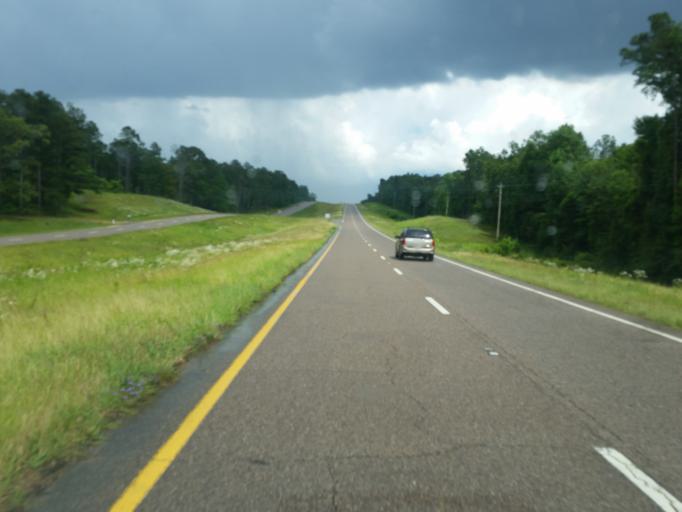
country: US
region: Mississippi
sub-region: George County
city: Lucedale
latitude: 30.9173
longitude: -88.4973
